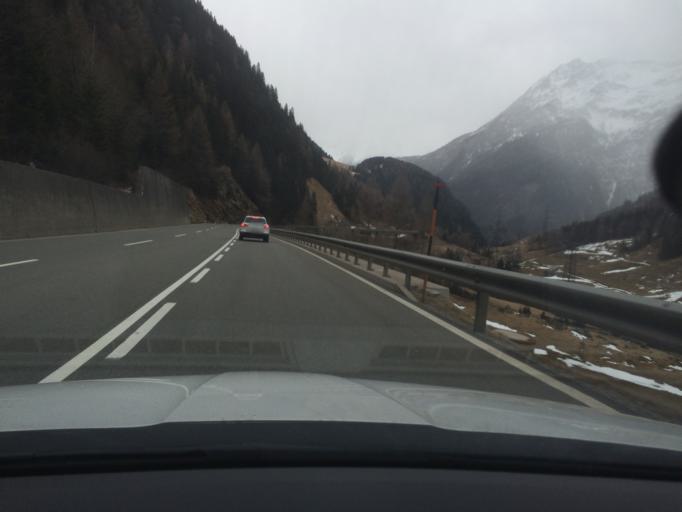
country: AT
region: Tyrol
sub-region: Politischer Bezirk Lienz
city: Matrei in Osttirol
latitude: 47.0694
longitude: 12.5320
